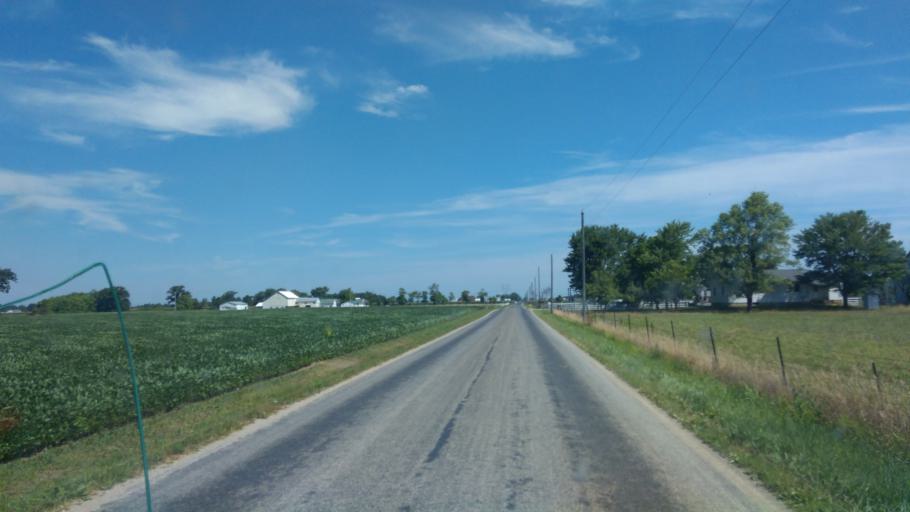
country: US
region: Indiana
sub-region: Adams County
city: Berne
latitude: 40.6982
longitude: -84.9750
